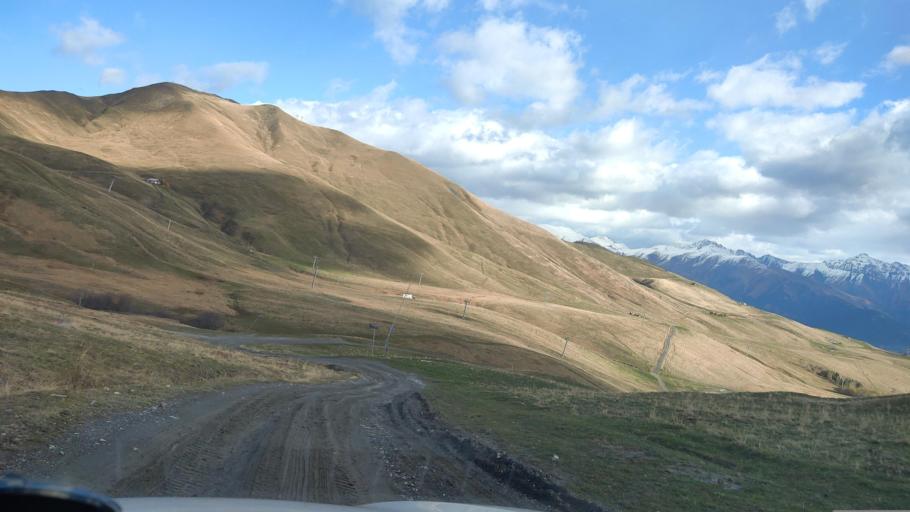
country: FR
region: Rhone-Alpes
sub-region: Departement de la Savoie
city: Saint-Etienne-de-Cuines
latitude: 45.2582
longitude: 6.2459
